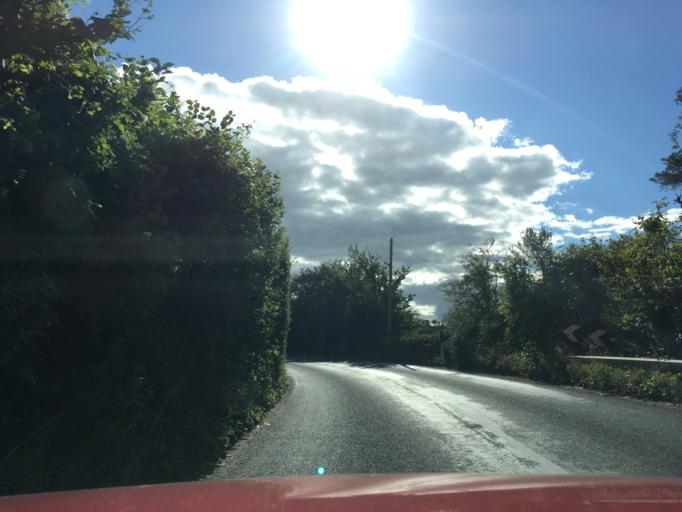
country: GB
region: England
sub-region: Devon
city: Buckfastleigh
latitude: 50.4322
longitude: -3.7573
